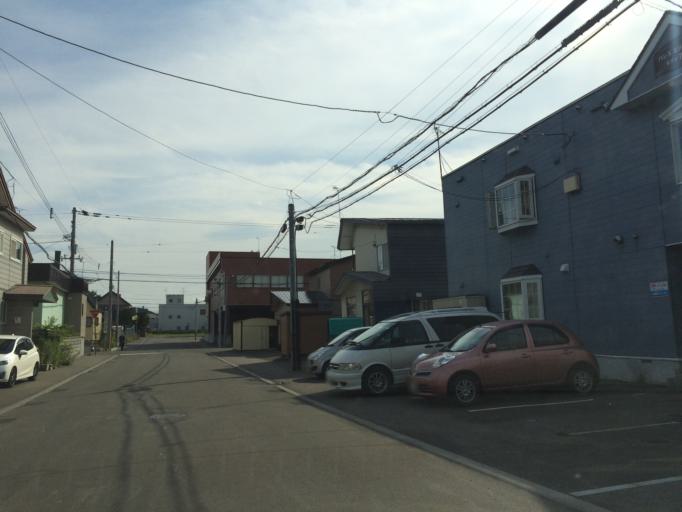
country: JP
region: Hokkaido
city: Ebetsu
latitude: 43.1124
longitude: 141.5495
